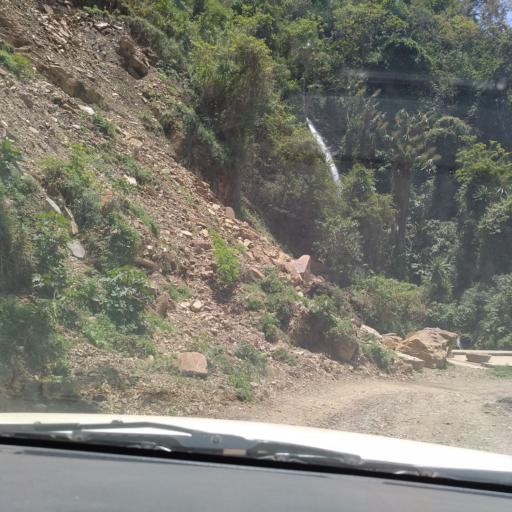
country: CD
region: Nord Kivu
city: Sake
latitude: -1.9169
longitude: 28.9457
